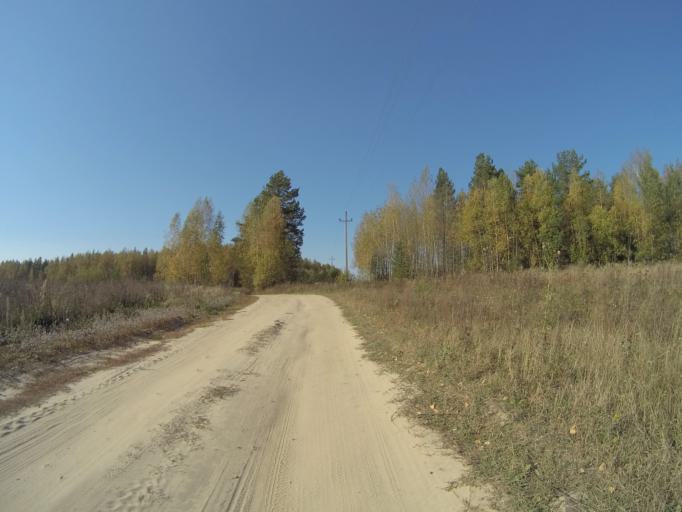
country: RU
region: Vladimir
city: Vorsha
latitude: 55.9834
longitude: 40.1975
